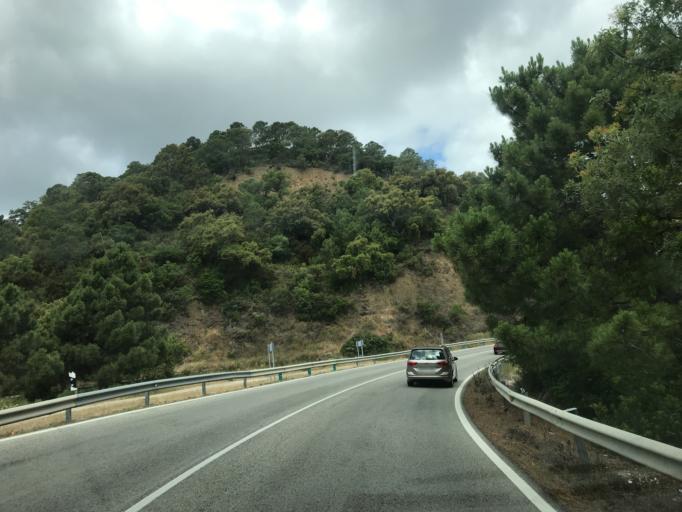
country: ES
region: Andalusia
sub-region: Provincia de Malaga
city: Benahavis
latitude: 36.5414
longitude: -5.0190
